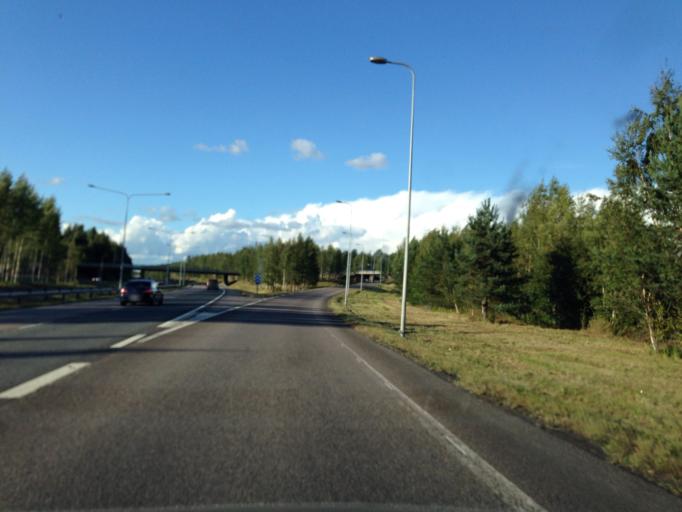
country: FI
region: Uusimaa
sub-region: Helsinki
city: Vantaa
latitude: 60.3385
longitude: 25.0010
